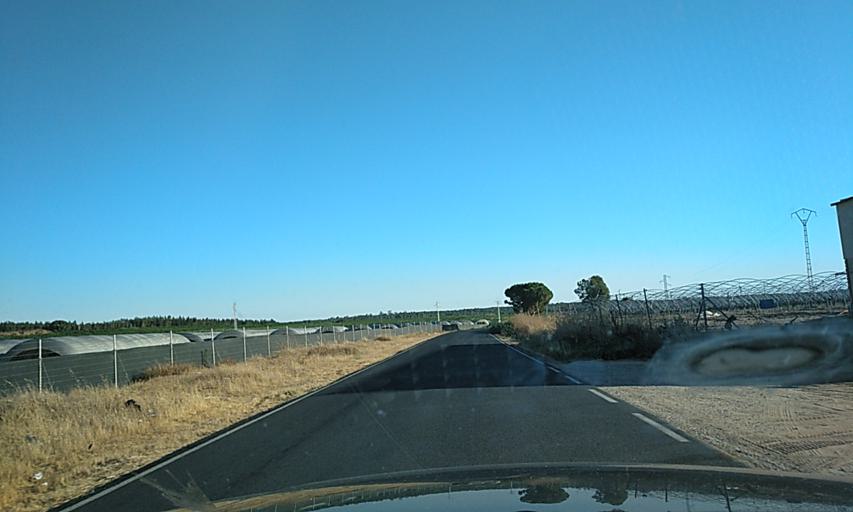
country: ES
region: Andalusia
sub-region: Provincia de Huelva
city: San Bartolome de la Torre
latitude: 37.4173
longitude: -7.1125
